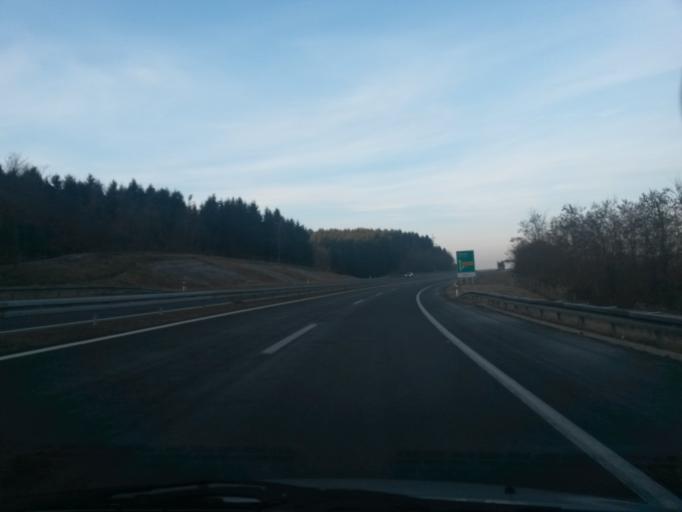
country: HR
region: Varazdinska
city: Jalzabet
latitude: 46.2455
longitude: 16.4011
